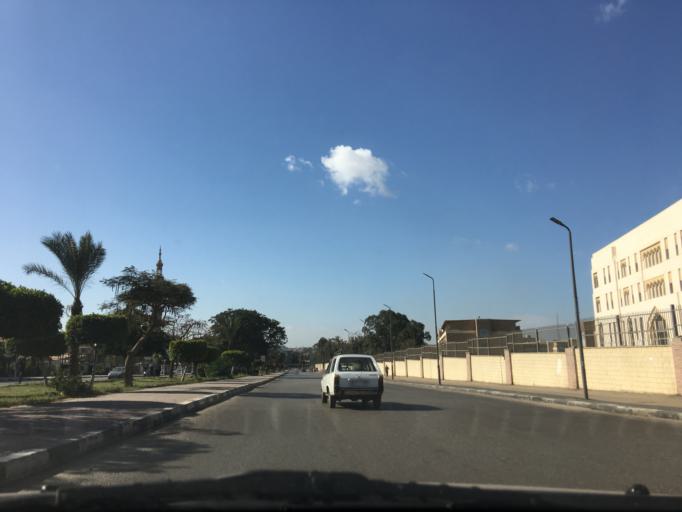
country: EG
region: Muhafazat al Qahirah
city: Cairo
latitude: 30.0518
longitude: 31.3231
